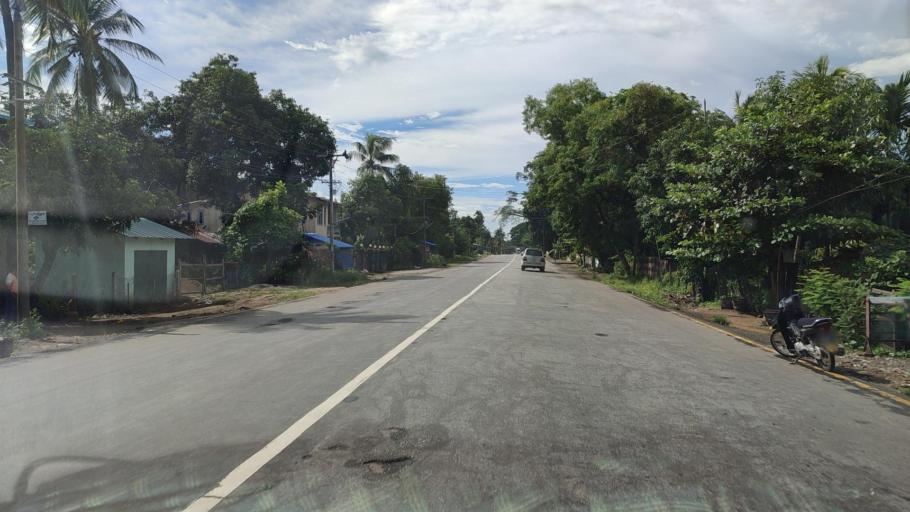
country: MM
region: Bago
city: Pyu
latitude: 18.3300
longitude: 96.4962
